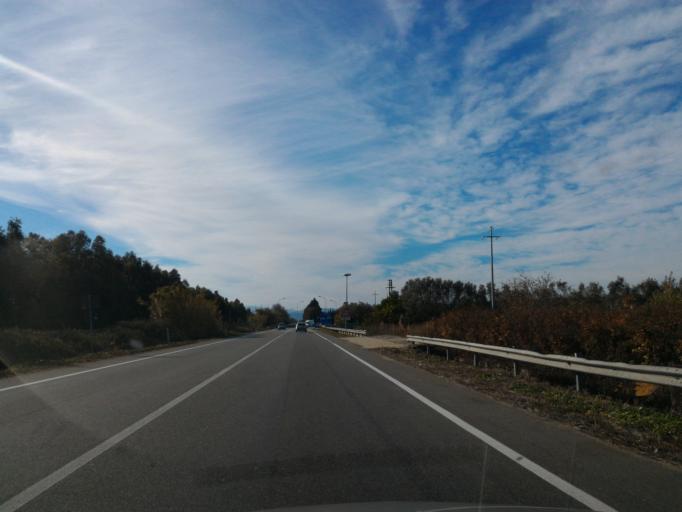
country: IT
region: Calabria
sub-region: Provincia di Catanzaro
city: Barone
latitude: 38.8598
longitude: 16.6768
